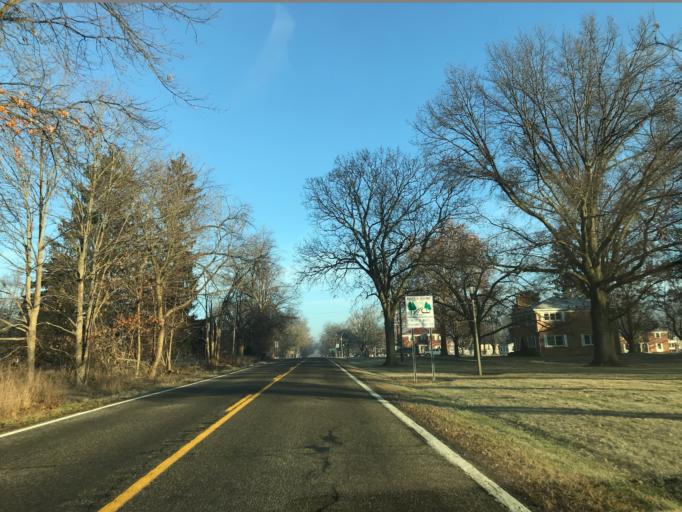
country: US
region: Michigan
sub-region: Eaton County
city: Eaton Rapids
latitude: 42.4728
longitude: -84.6008
